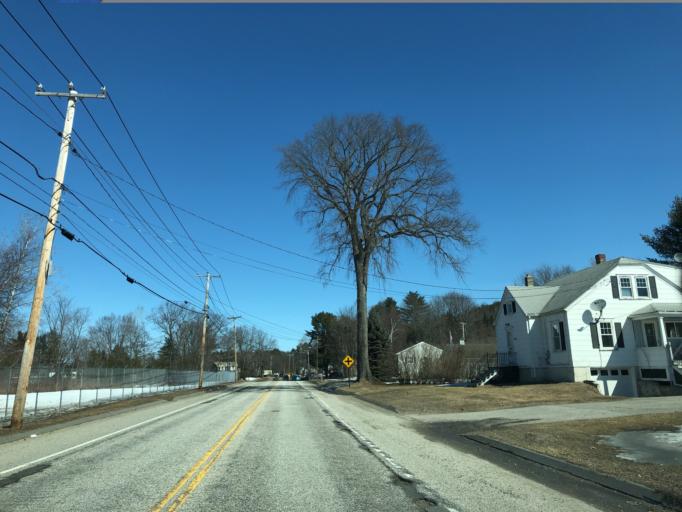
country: US
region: Maine
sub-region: Androscoggin County
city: Minot
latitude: 44.0493
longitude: -70.2765
